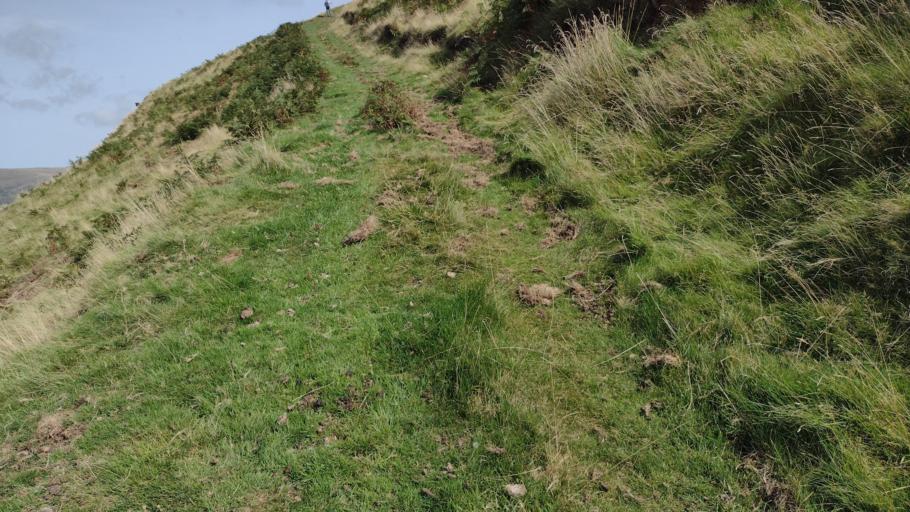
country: GB
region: Wales
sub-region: Gwynedd
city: Barmouth
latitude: 52.6535
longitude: -3.9678
